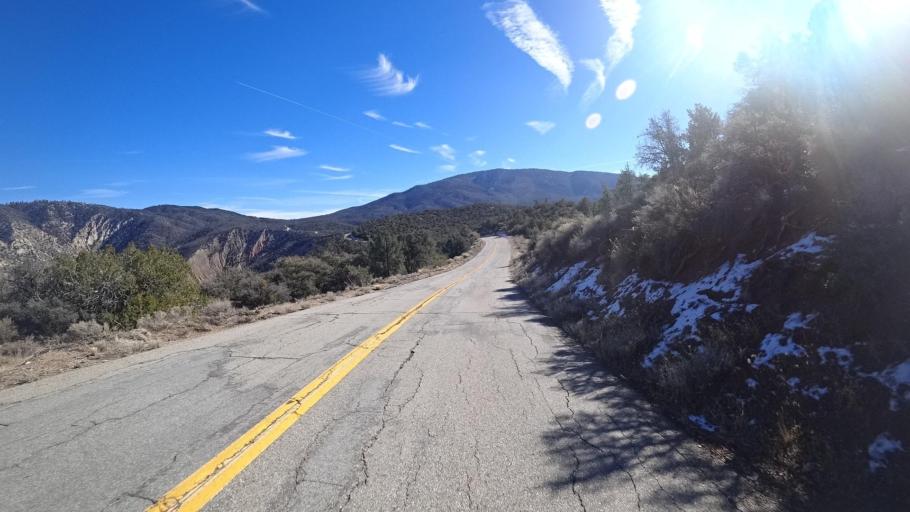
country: US
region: California
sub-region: Kern County
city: Pine Mountain Club
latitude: 34.8670
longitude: -119.2586
